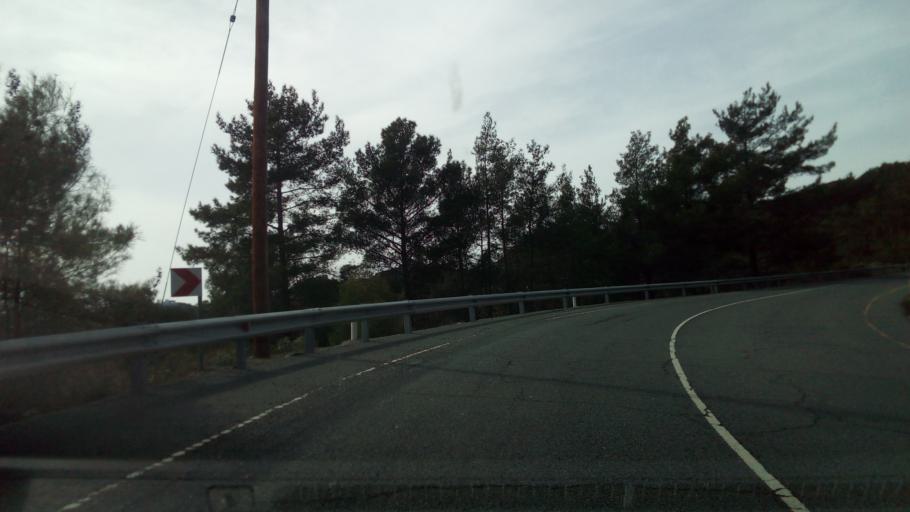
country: CY
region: Limassol
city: Pelendri
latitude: 34.8856
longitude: 32.9534
